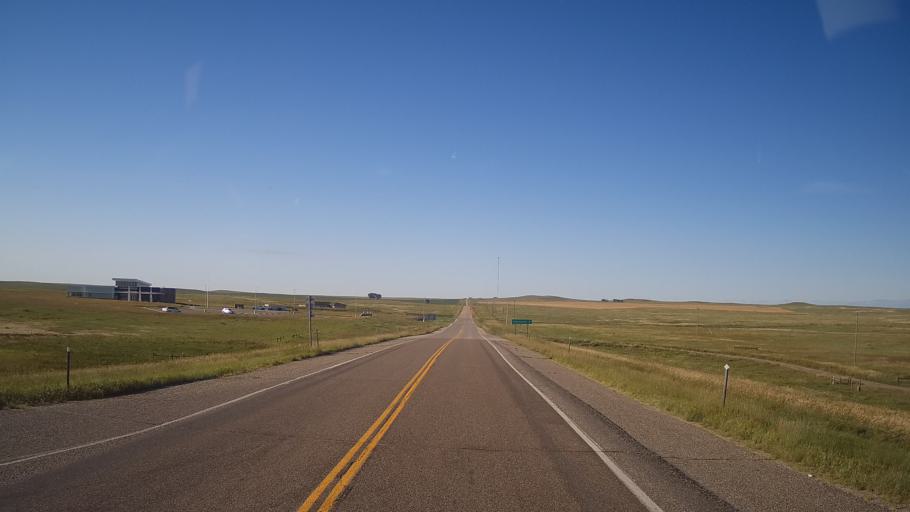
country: US
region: South Dakota
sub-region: Haakon County
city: Philip
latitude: 43.8419
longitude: -101.8997
